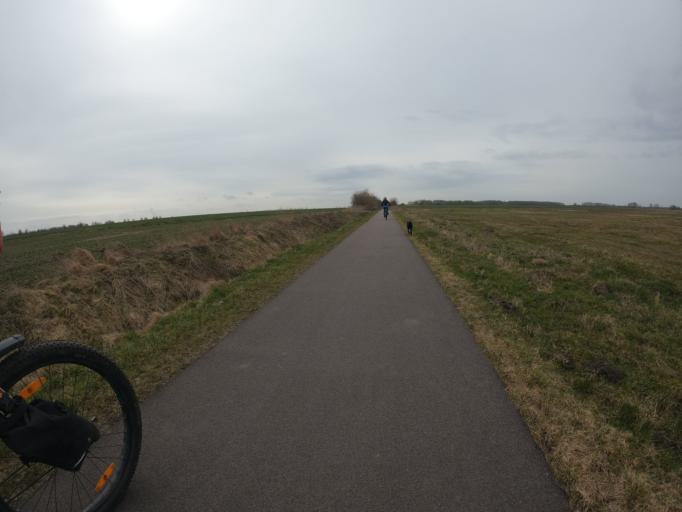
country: PL
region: West Pomeranian Voivodeship
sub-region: Powiat gryficki
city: Mrzezyno
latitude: 54.1170
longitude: 15.3039
